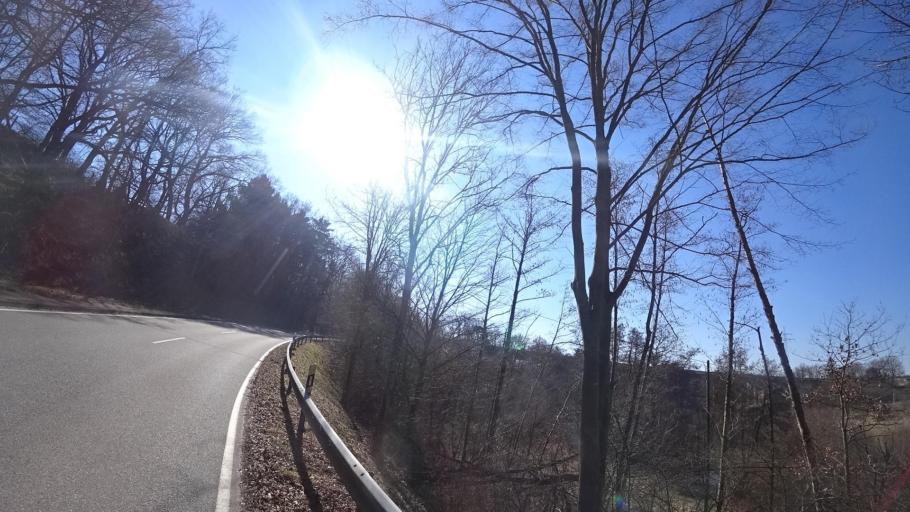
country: DE
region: Rheinland-Pfalz
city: Unzenberg
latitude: 49.9609
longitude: 7.4564
